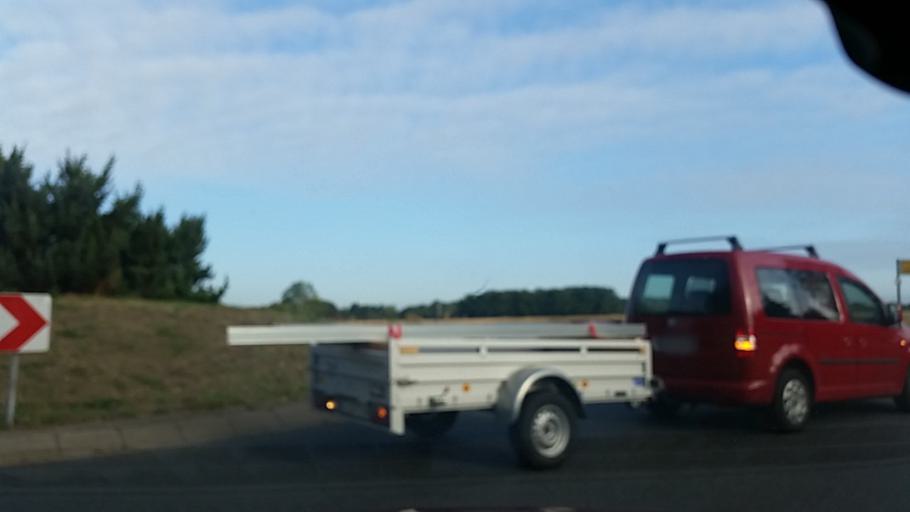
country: DE
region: Lower Saxony
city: Lachendorf
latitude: 52.6326
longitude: 10.2237
